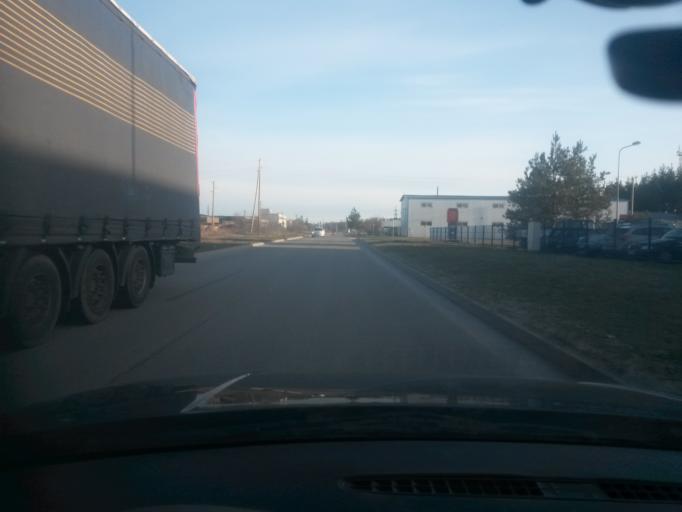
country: LV
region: Stopini
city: Ulbroka
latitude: 56.9086
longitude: 24.2461
